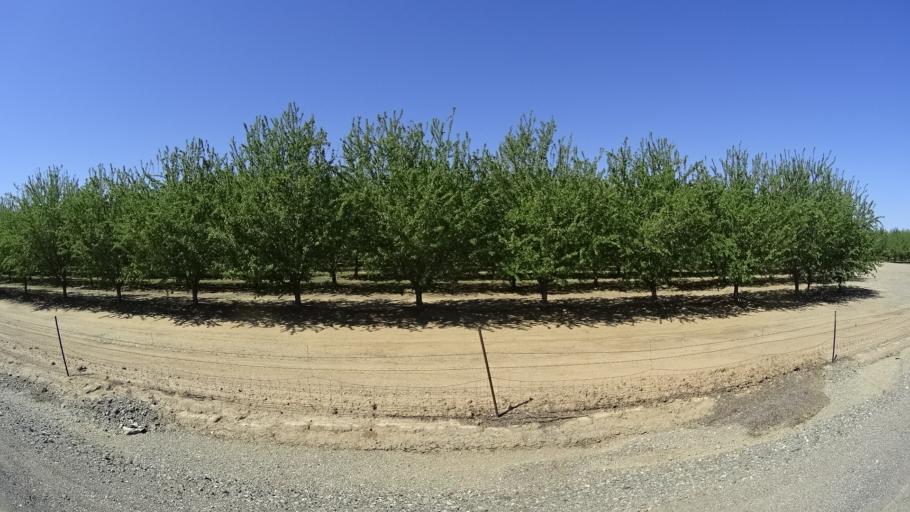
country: US
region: California
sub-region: Glenn County
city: Orland
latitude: 39.6454
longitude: -122.2347
